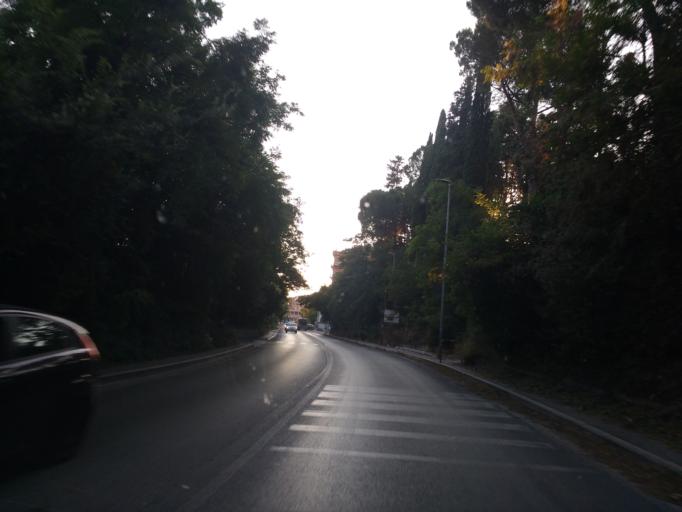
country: IT
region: Latium
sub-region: Citta metropolitana di Roma Capitale
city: Villanova
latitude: 41.9569
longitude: 12.7607
